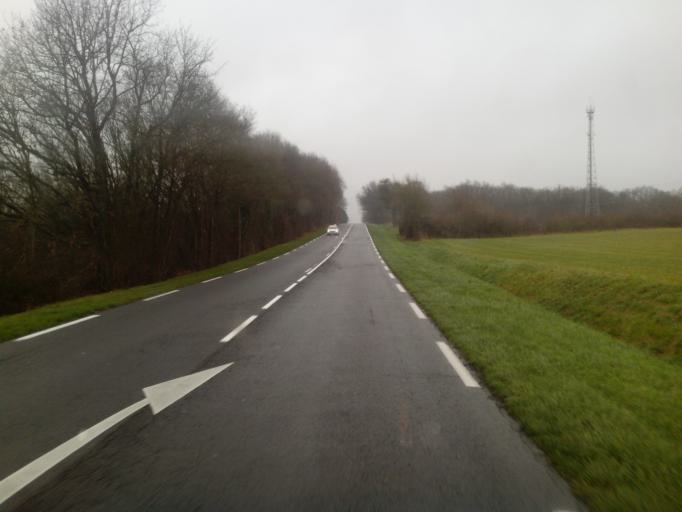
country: FR
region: Poitou-Charentes
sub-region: Departement de la Vienne
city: Terce
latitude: 46.4405
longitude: 0.5863
